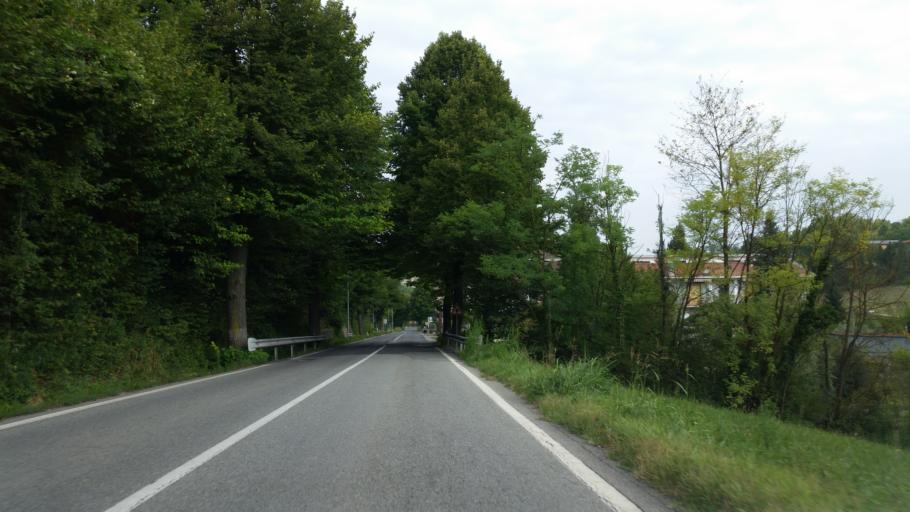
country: IT
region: Piedmont
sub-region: Provincia di Torino
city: Brozolo
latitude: 45.1311
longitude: 8.0580
